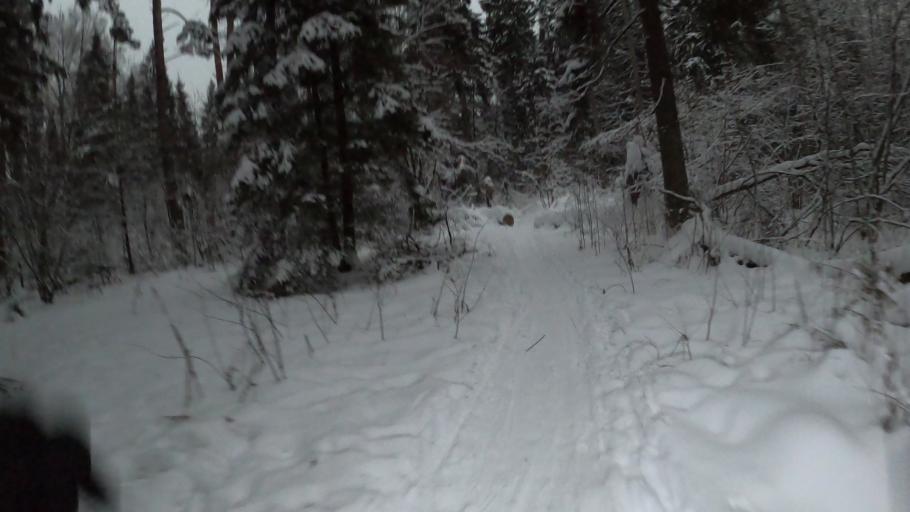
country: RU
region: Moskovskaya
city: Nakhabino
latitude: 55.8930
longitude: 37.2092
